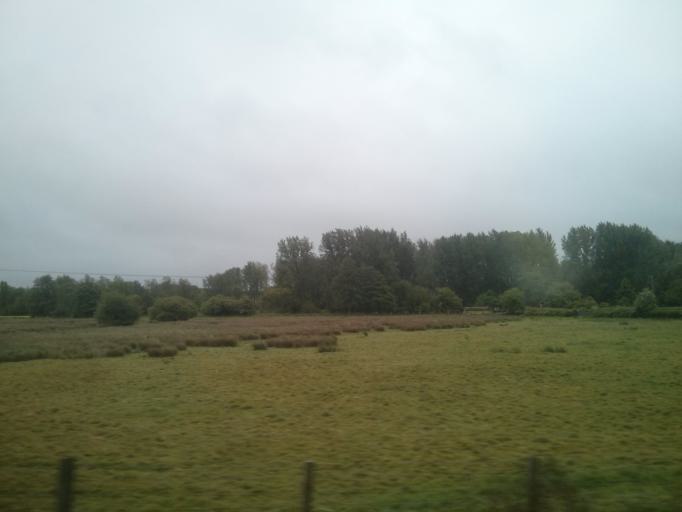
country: GB
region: England
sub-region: West Berkshire
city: Theale
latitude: 51.4151
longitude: -1.1136
